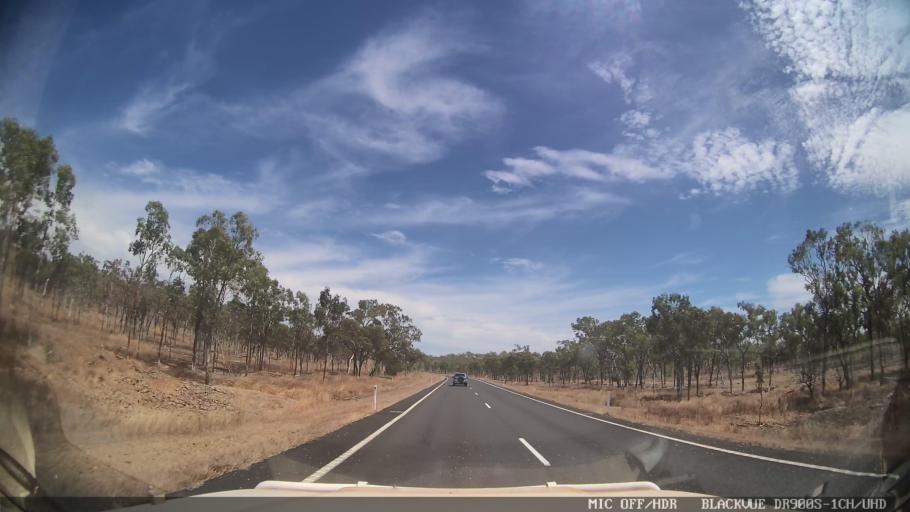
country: AU
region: Queensland
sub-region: Cook
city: Cooktown
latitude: -15.7590
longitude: 144.9958
